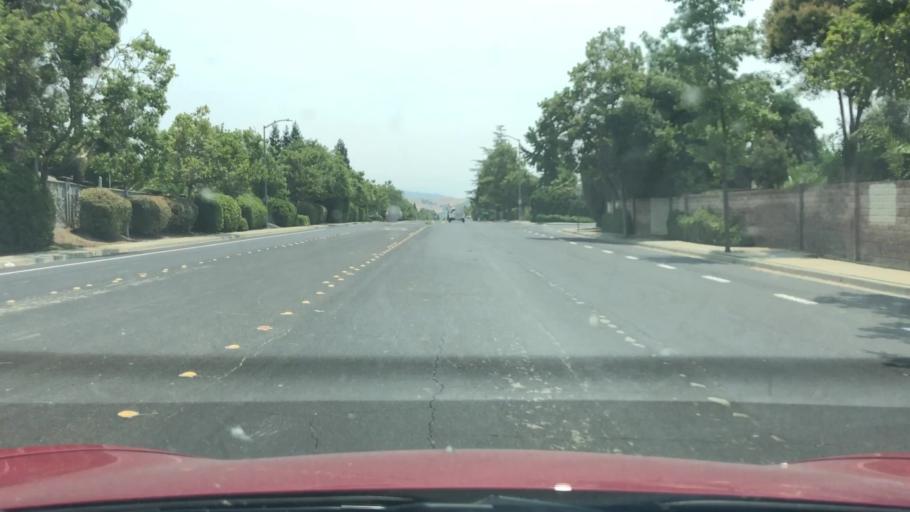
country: US
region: California
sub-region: Alameda County
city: Livermore
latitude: 37.6640
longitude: -121.7682
